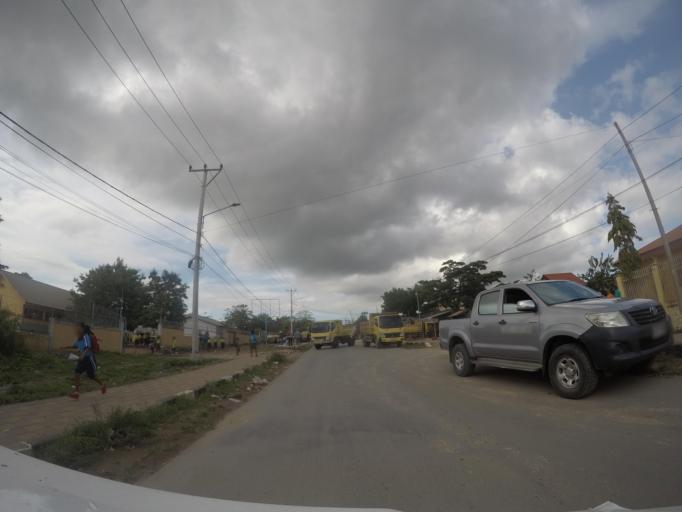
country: TL
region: Baucau
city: Baucau
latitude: -8.4780
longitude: 126.4542
